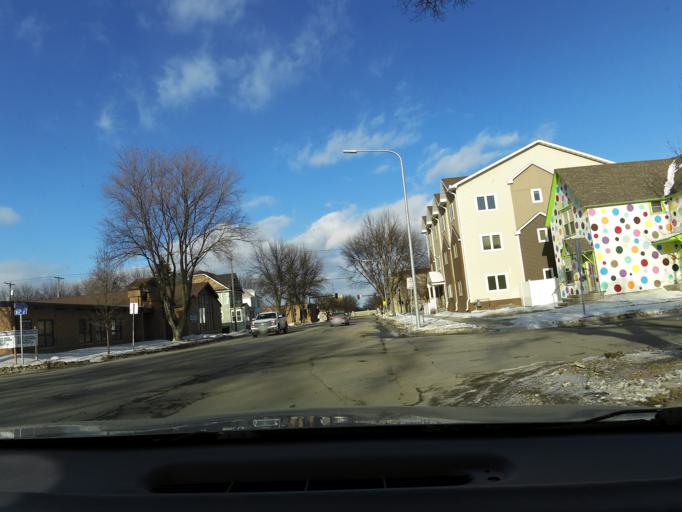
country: US
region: North Dakota
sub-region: Grand Forks County
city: Grand Forks
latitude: 47.9248
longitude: -97.0371
